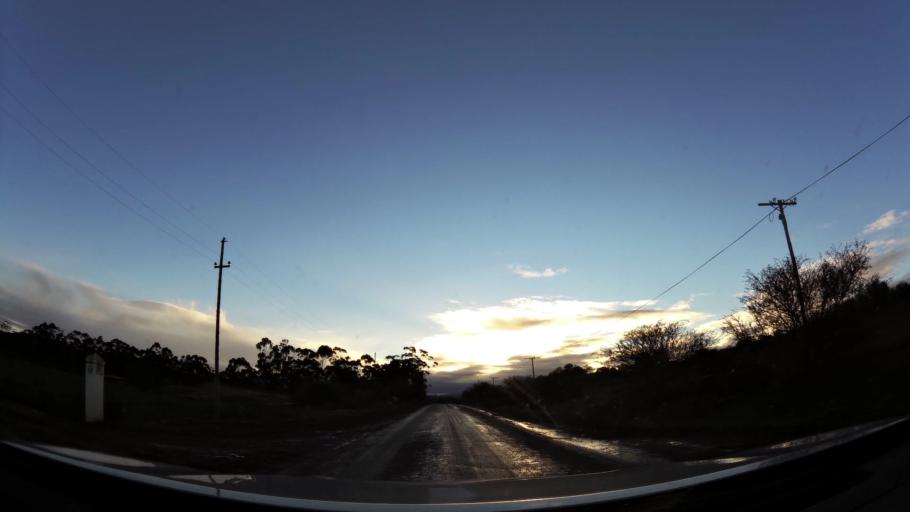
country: ZA
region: Western Cape
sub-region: Eden District Municipality
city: Riversdale
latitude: -34.0819
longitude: 20.9425
